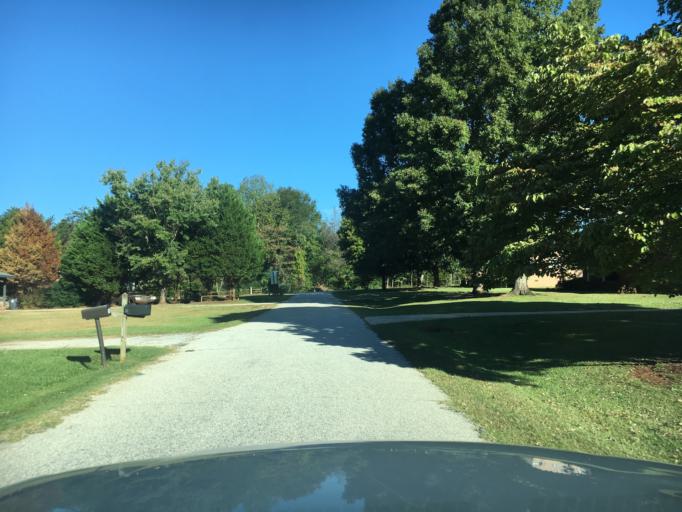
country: US
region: South Carolina
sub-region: Spartanburg County
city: Lyman
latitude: 34.9257
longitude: -82.1230
